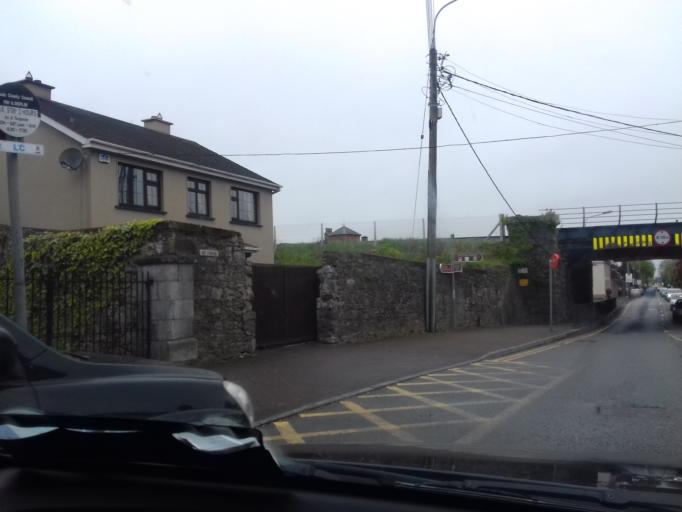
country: IE
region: Leinster
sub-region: Laois
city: Portlaoise
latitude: 53.0351
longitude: -7.3035
